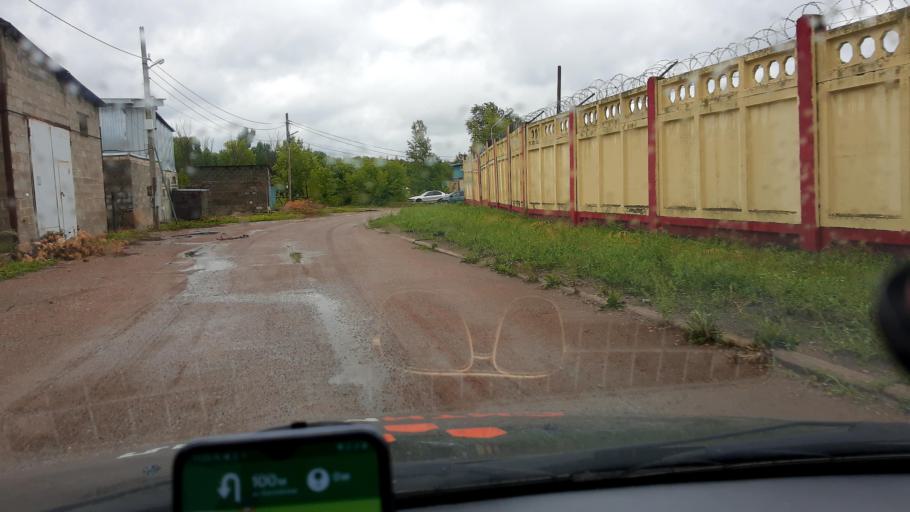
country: RU
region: Bashkortostan
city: Ufa
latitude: 54.7960
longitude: 56.0996
